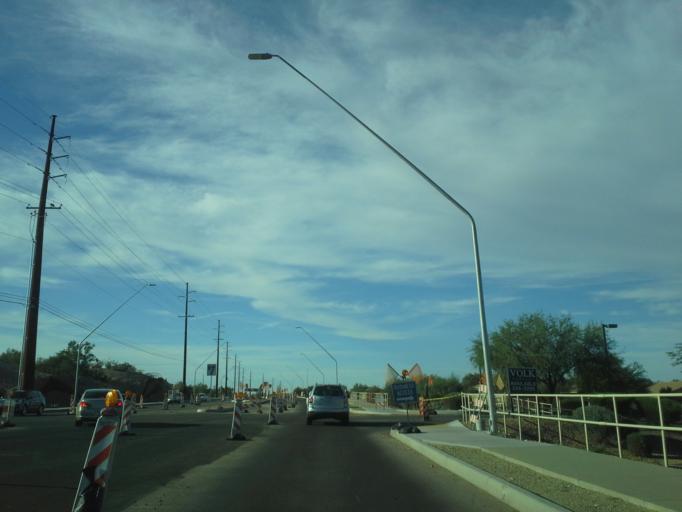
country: US
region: Arizona
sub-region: Pima County
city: Flowing Wells
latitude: 32.2526
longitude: -111.0144
